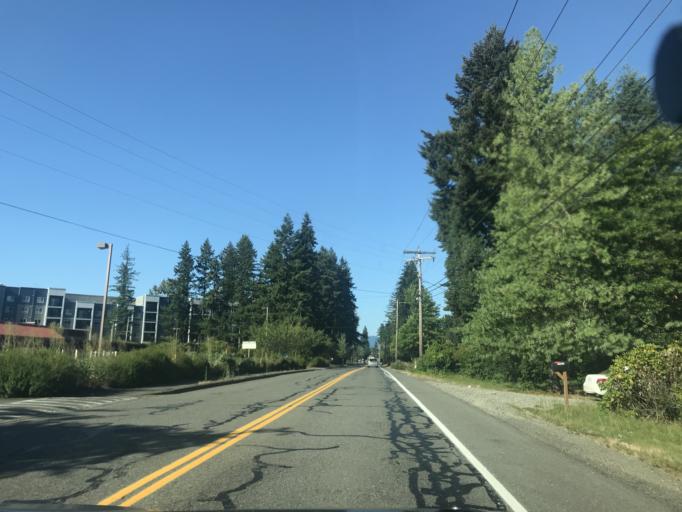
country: US
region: Washington
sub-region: King County
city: Covington
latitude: 47.3531
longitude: -122.1136
